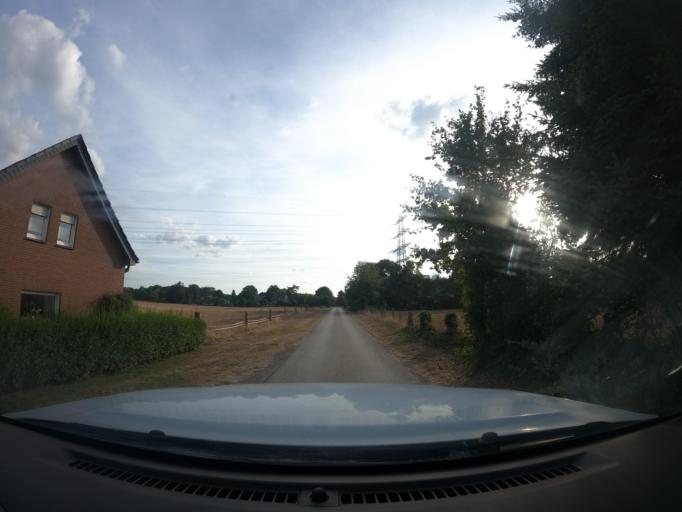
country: DE
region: North Rhine-Westphalia
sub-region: Regierungsbezirk Dusseldorf
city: Hamminkeln
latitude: 51.7031
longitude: 6.5947
